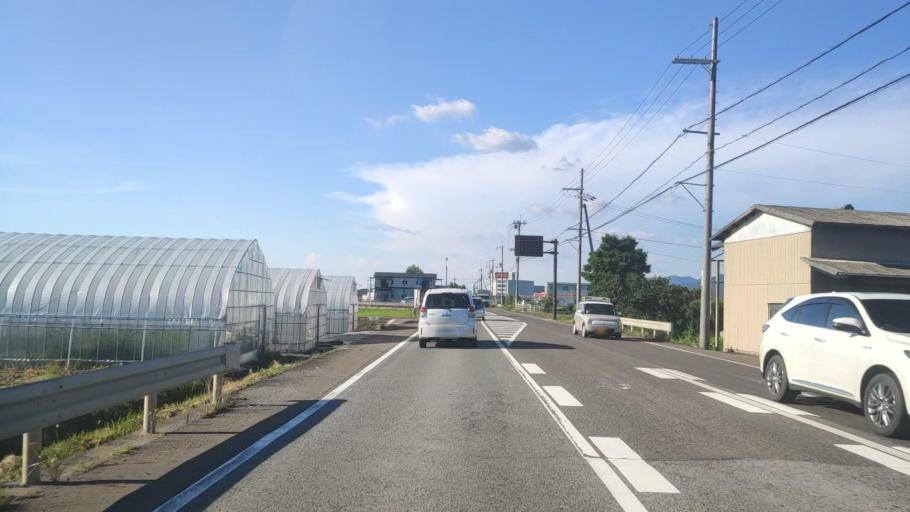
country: JP
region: Shiga Prefecture
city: Youkaichi
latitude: 35.0785
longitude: 136.2492
